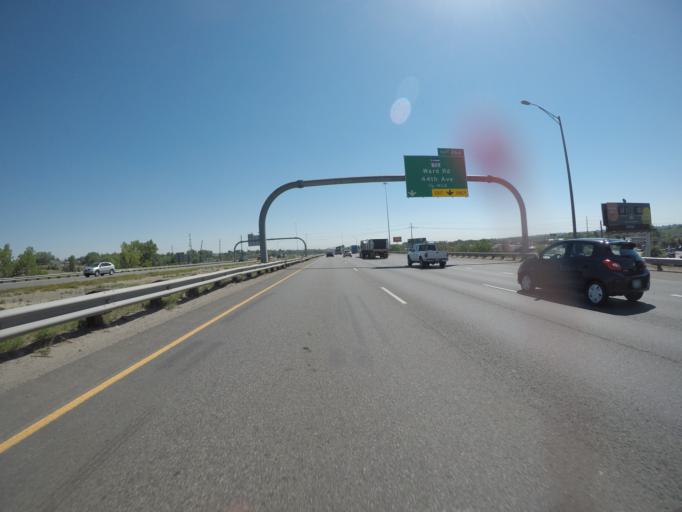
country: US
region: Colorado
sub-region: Jefferson County
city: Applewood
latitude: 39.7790
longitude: -105.1395
